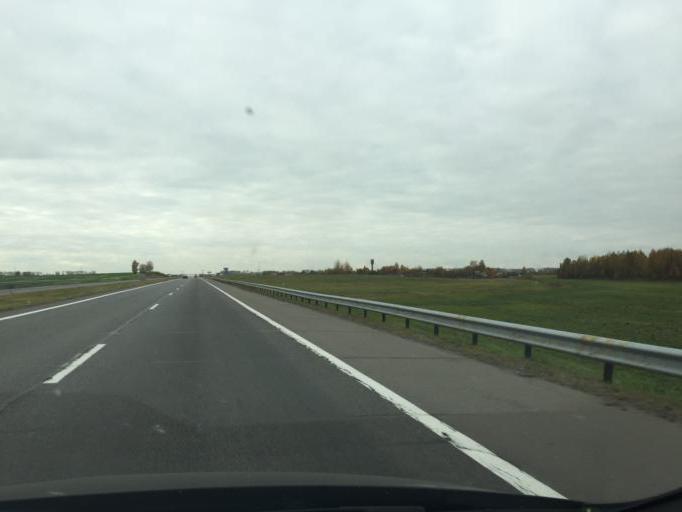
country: BY
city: Fanipol
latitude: 53.6965
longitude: 27.3998
